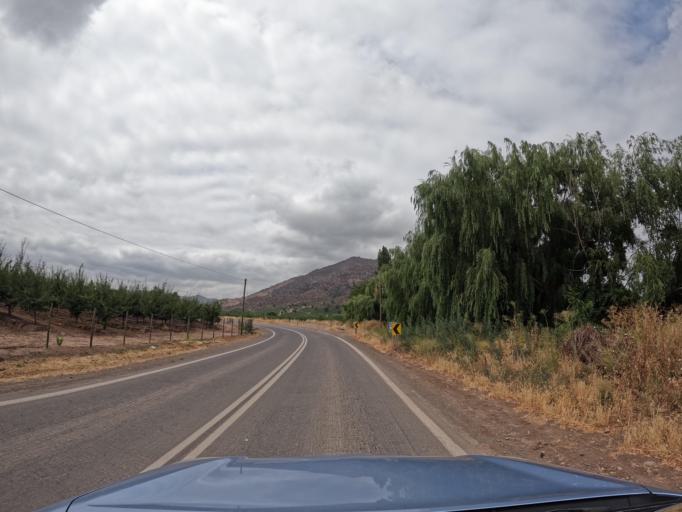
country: CL
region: Maule
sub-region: Provincia de Curico
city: Teno
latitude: -34.7562
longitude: -71.2174
